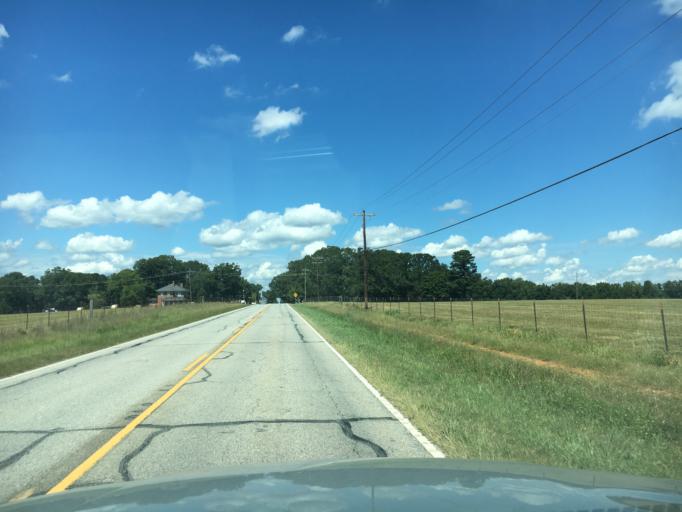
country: US
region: South Carolina
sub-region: Laurens County
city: Laurens
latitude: 34.5081
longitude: -82.0817
